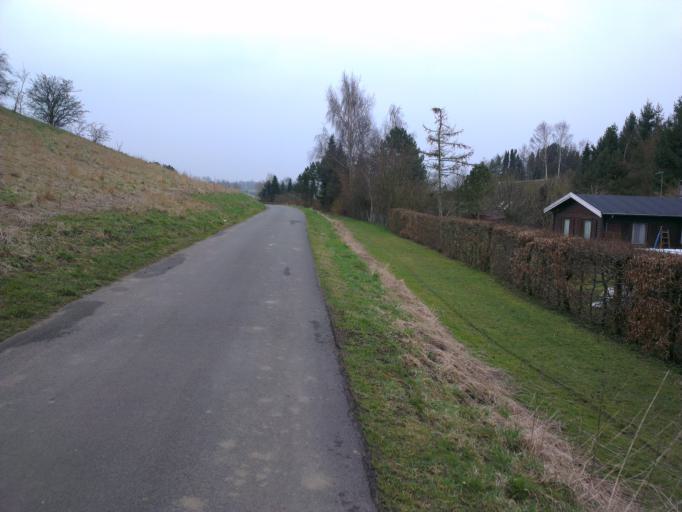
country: DK
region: Zealand
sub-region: Lejre Kommune
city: Ejby
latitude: 55.7403
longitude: 11.8678
